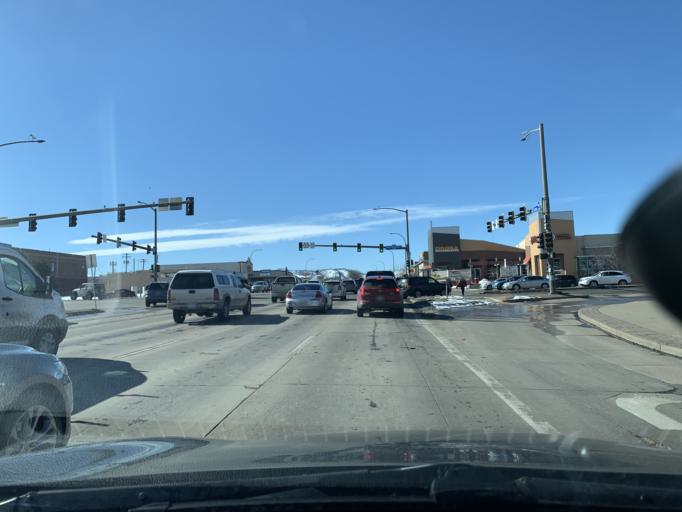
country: US
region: Colorado
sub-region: Jefferson County
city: Edgewater
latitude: 39.7404
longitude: -105.0807
